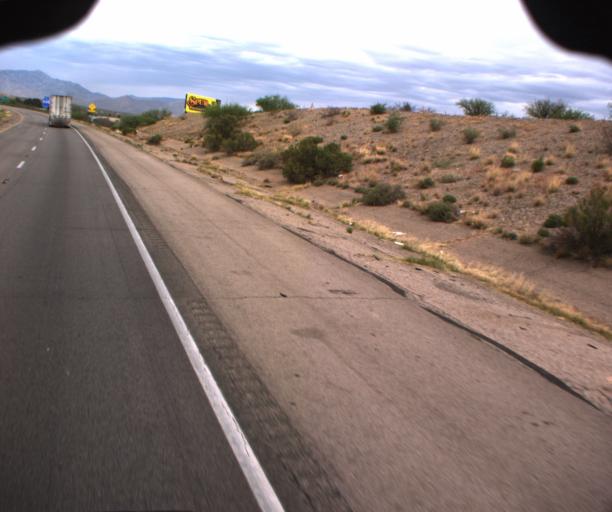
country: US
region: Arizona
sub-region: Cochise County
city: Benson
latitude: 31.9758
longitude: -110.2891
